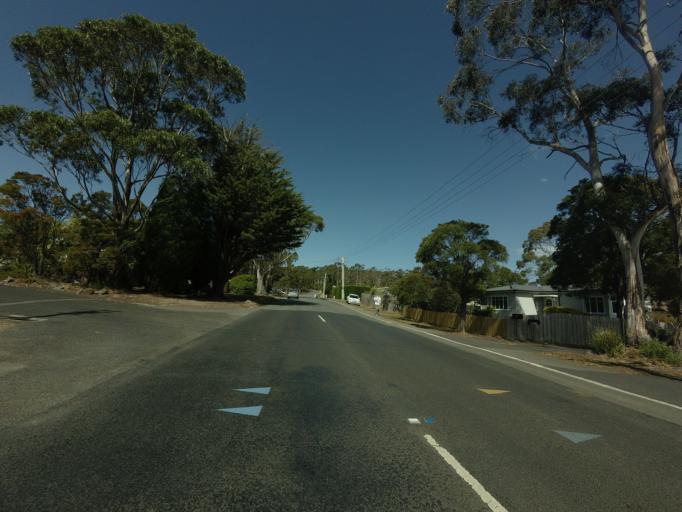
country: AU
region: Tasmania
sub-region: Hobart
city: Dynnyrne
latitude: -42.9242
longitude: 147.3273
